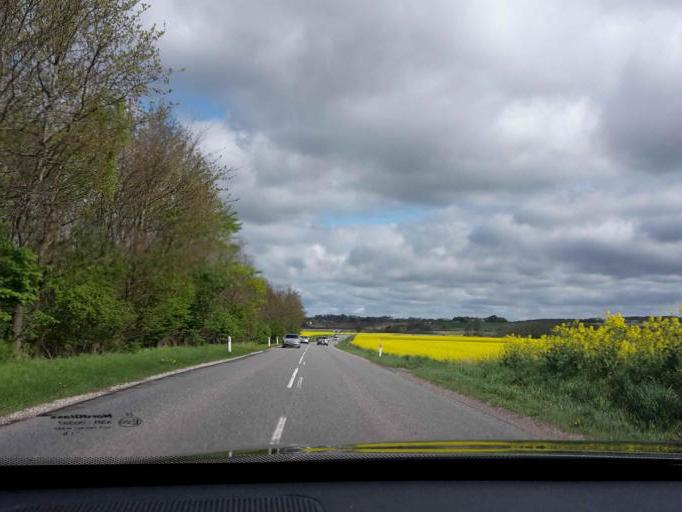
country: DK
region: Central Jutland
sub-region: Syddjurs Kommune
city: Hornslet
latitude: 56.3357
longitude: 10.3352
